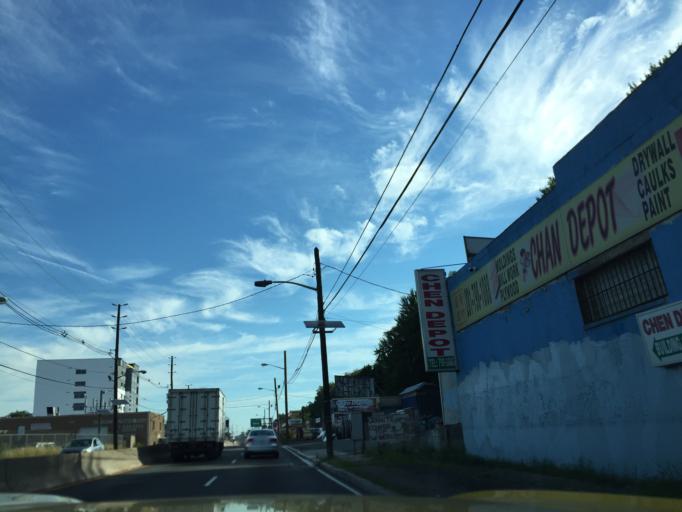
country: US
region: New Jersey
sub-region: Hudson County
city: Hoboken
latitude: 40.7530
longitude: -74.0572
